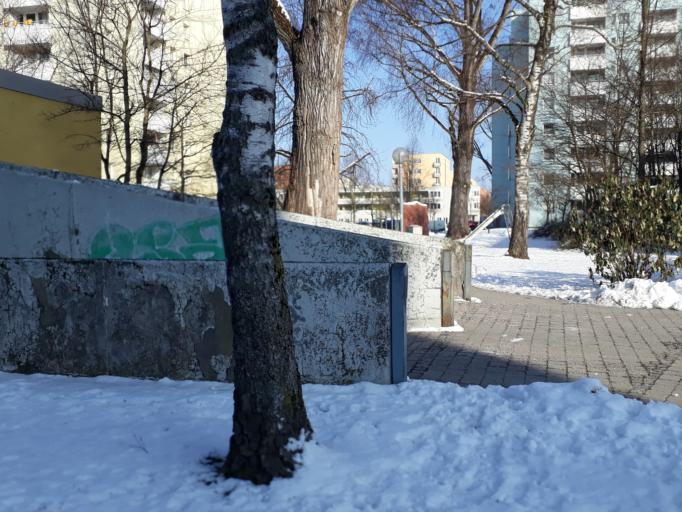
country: DE
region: Bavaria
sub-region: Upper Bavaria
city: Oberschleissheim
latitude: 48.2079
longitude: 11.5672
